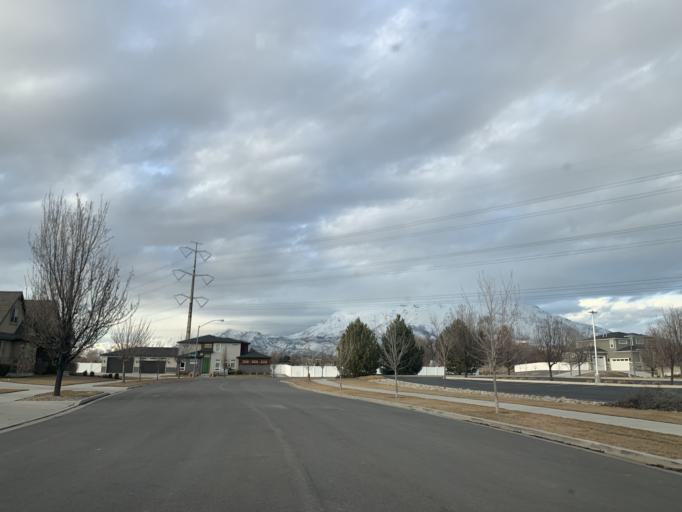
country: US
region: Utah
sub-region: Utah County
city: Orem
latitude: 40.2528
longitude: -111.7114
